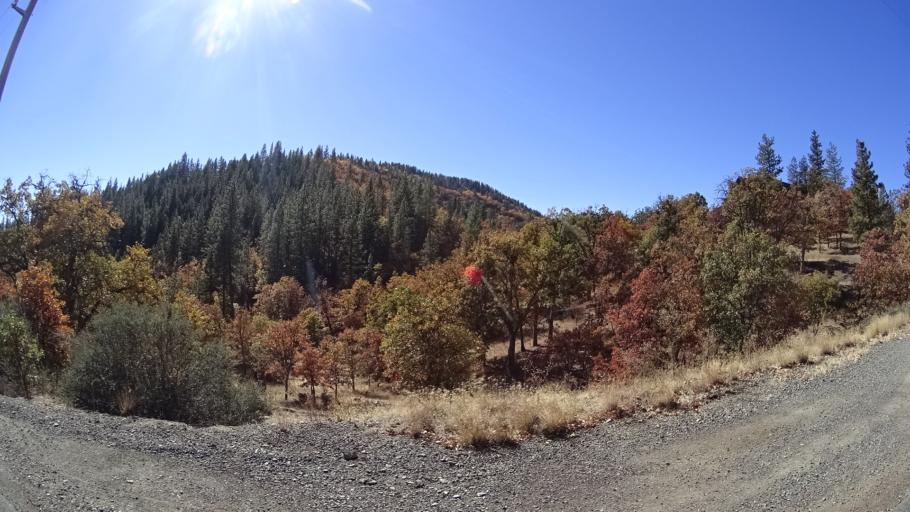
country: US
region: California
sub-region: Siskiyou County
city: Yreka
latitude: 41.5665
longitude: -122.9369
